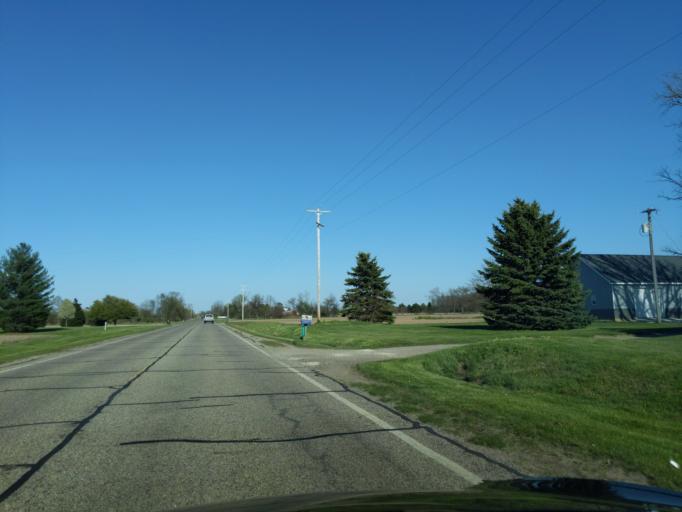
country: US
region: Michigan
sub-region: Ionia County
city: Portland
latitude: 42.8858
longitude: -85.0085
